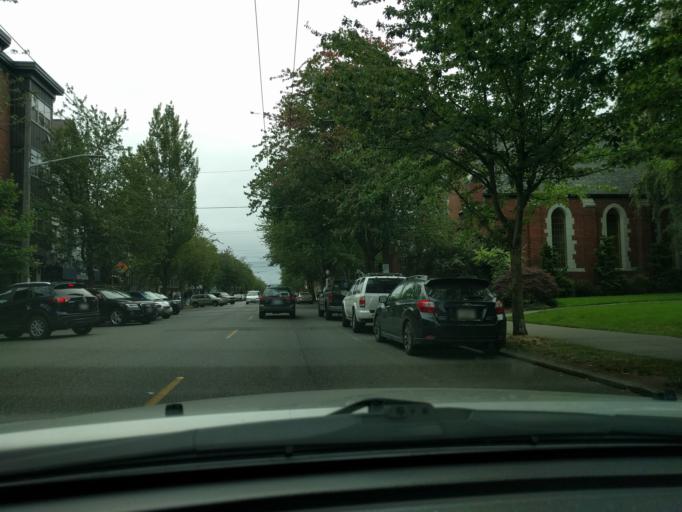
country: US
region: Washington
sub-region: King County
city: Seattle
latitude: 47.6350
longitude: -122.3569
